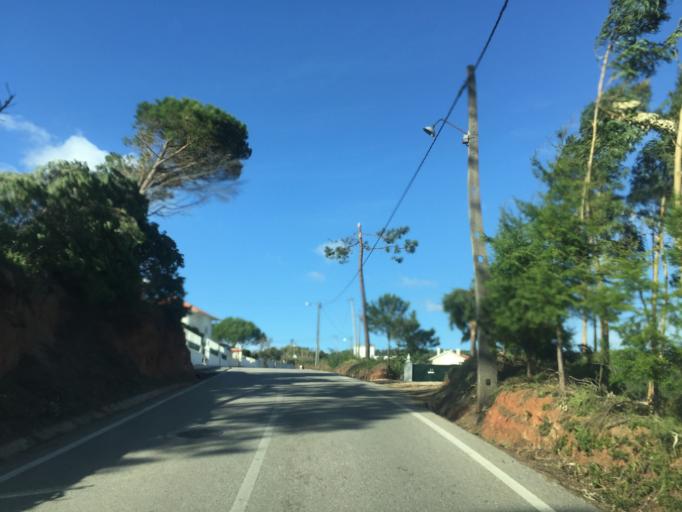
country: PT
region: Coimbra
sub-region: Figueira da Foz
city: Tavarede
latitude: 40.1785
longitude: -8.8372
